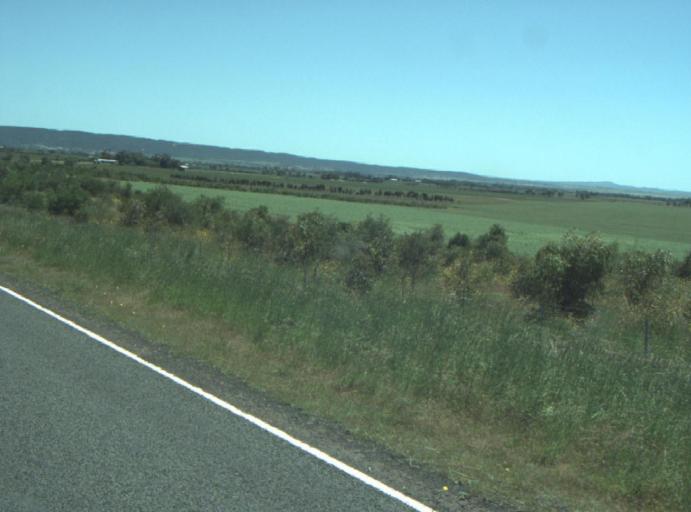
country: AU
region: Victoria
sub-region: Greater Geelong
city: Lara
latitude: -37.8846
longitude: 144.3401
